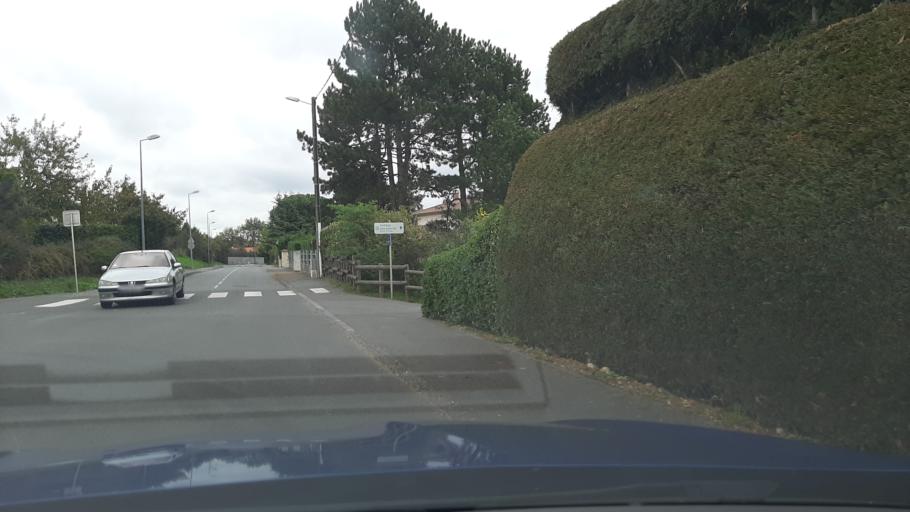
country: FR
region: Rhone-Alpes
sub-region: Departement du Rhone
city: Belleville
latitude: 46.1092
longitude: 4.7221
